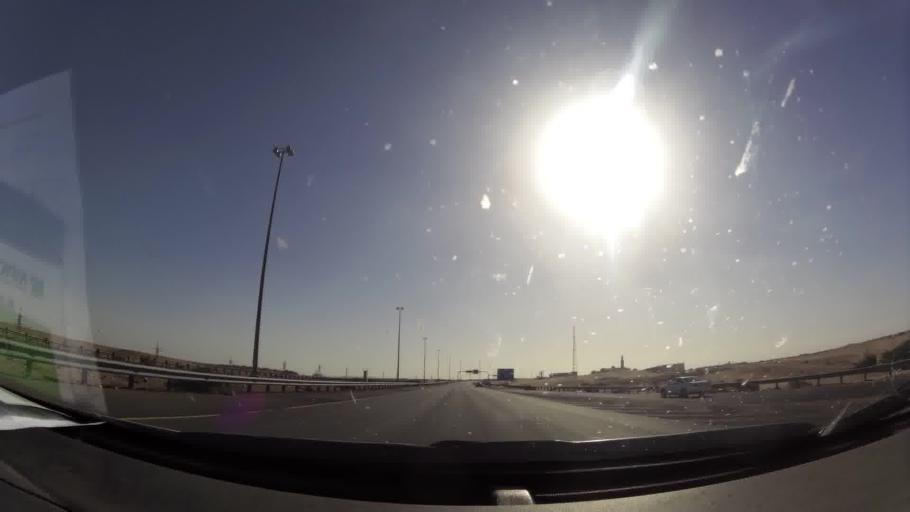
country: KW
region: Al Asimah
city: Kuwait City
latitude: 29.5833
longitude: 47.9056
